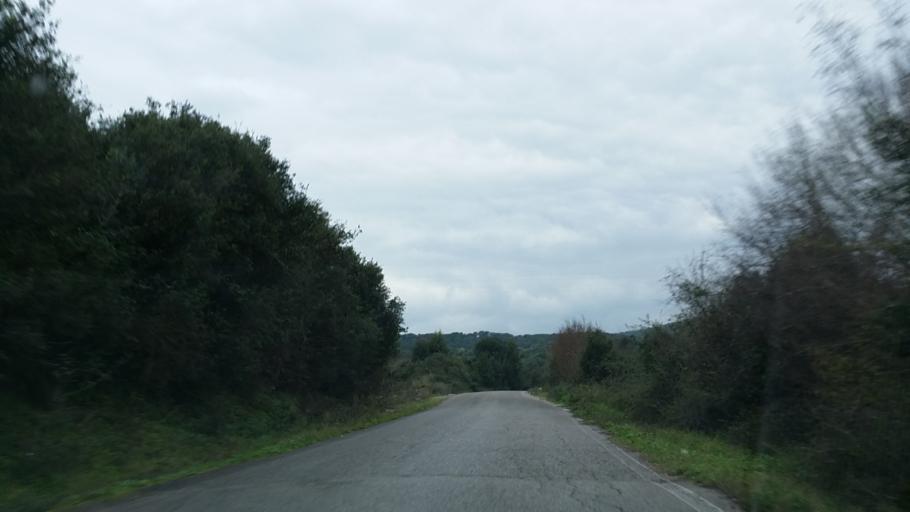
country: GR
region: West Greece
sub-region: Nomos Aitolias kai Akarnanias
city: Fitiai
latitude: 38.7197
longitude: 21.1826
